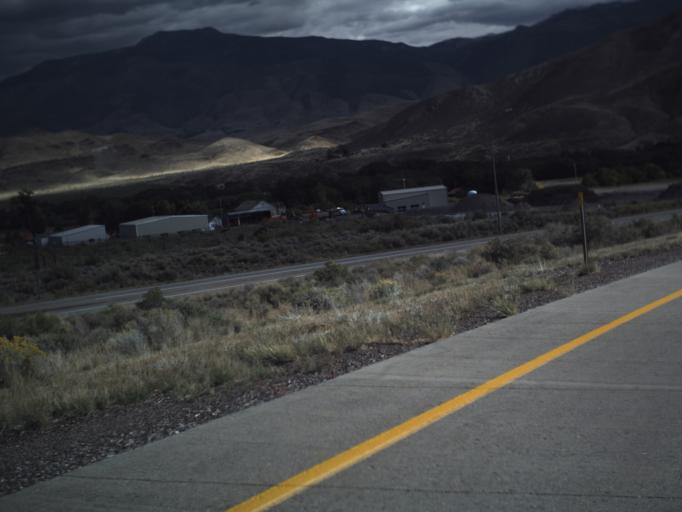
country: US
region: Utah
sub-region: Sevier County
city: Monroe
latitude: 38.5973
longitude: -112.2554
